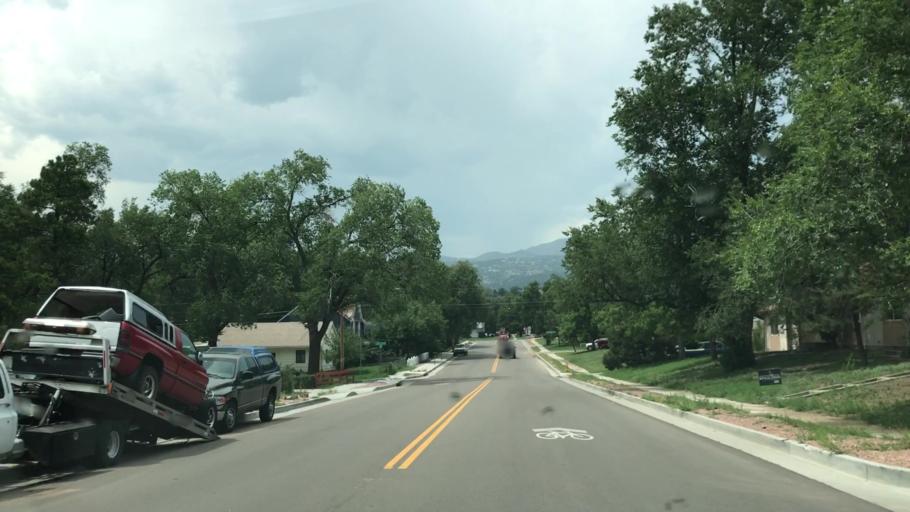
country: US
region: Colorado
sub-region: El Paso County
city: Colorado Springs
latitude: 38.8539
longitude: -104.8647
